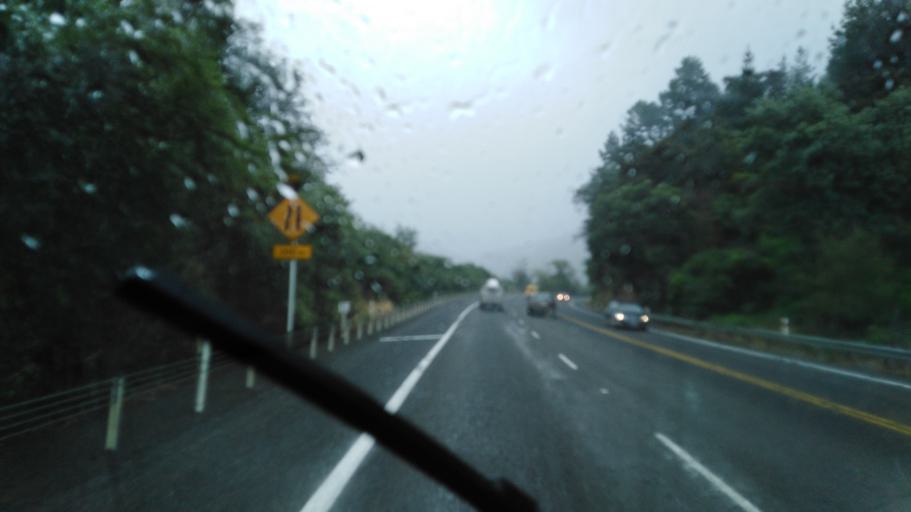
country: NZ
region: Marlborough
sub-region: Marlborough District
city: Picton
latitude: -41.3804
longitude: 173.9477
